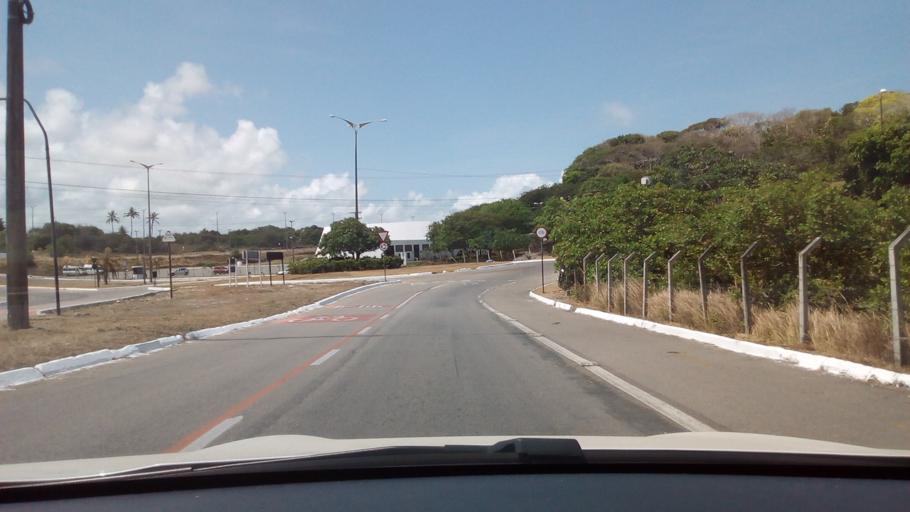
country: BR
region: Paraiba
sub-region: Joao Pessoa
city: Joao Pessoa
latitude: -7.1504
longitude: -34.7969
